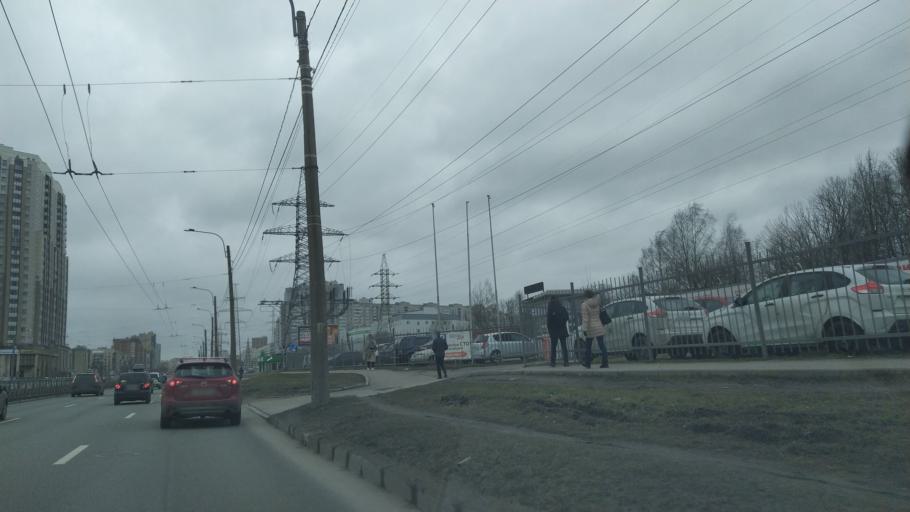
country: RU
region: Leningrad
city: Chernaya Rechka
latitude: 60.0020
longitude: 30.3063
